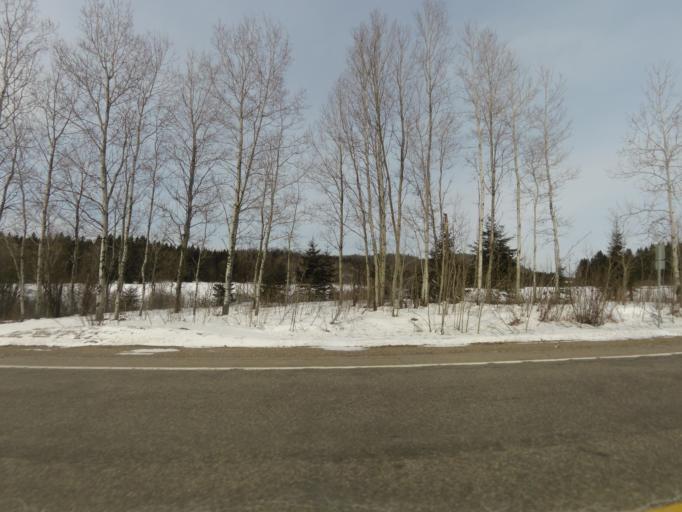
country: CA
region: Quebec
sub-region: Laurentides
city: Mont-Laurier
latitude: 46.3386
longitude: -75.5327
